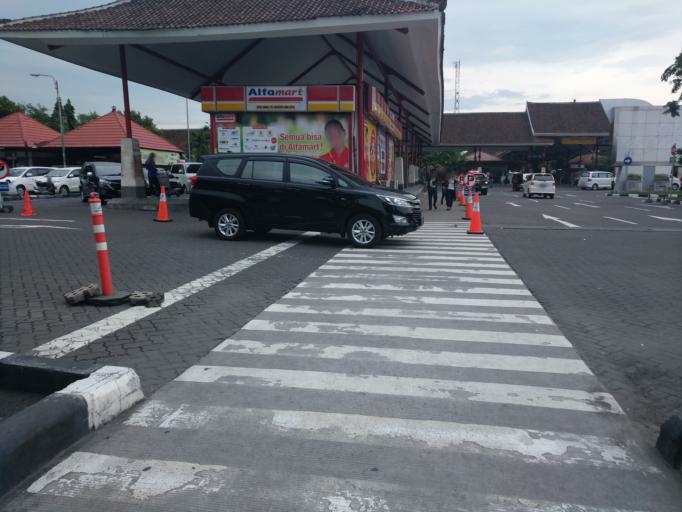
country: ID
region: Bali
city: Kelanabian
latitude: -8.7418
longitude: 115.1640
